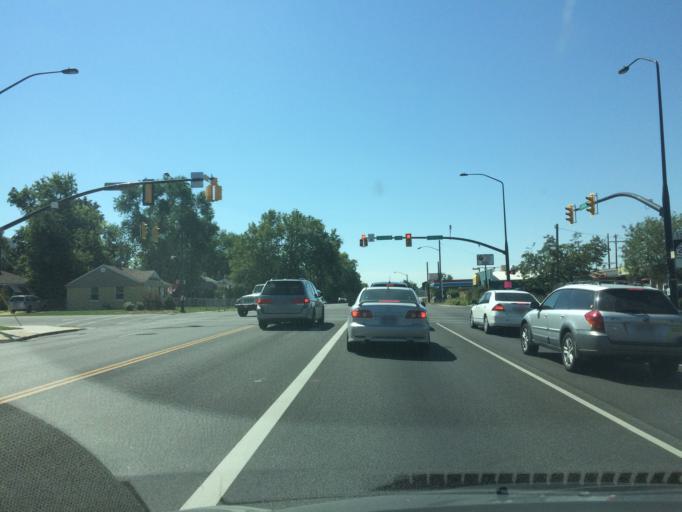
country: US
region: Utah
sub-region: Weber County
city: Ogden
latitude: 41.2104
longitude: -111.9485
